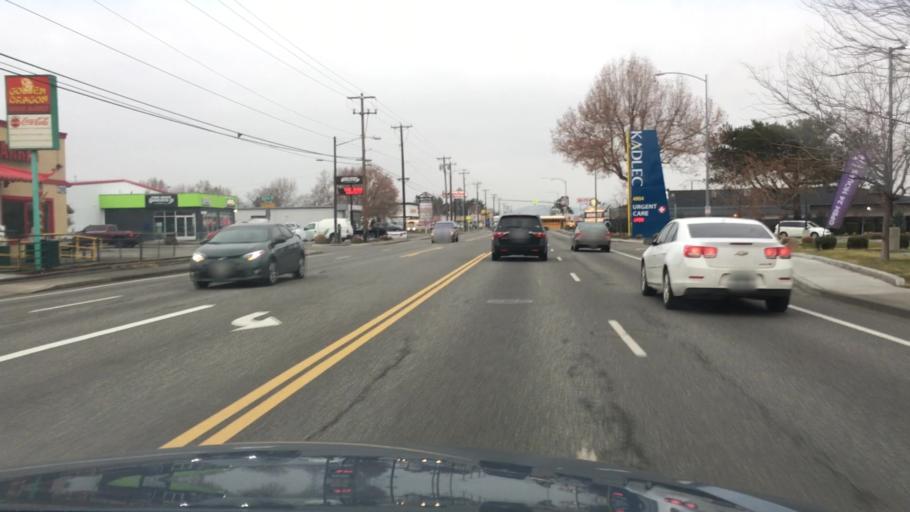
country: US
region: Washington
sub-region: Franklin County
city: West Pasco
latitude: 46.2125
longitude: -119.1839
